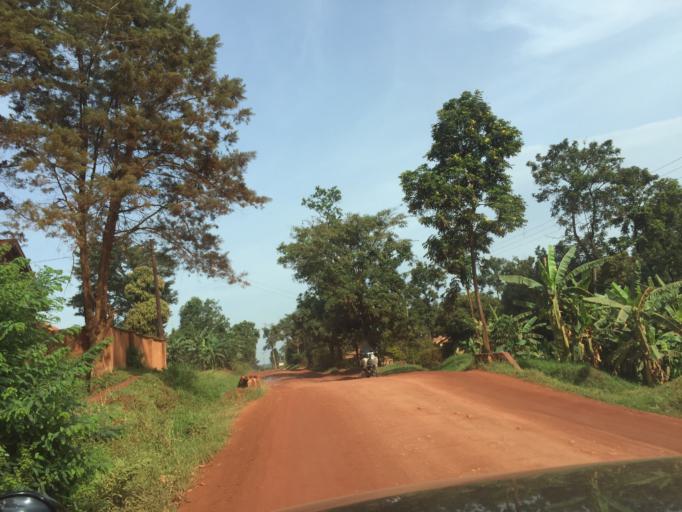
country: UG
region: Central Region
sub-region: Wakiso District
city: Wakiso
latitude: 0.4651
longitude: 32.5420
